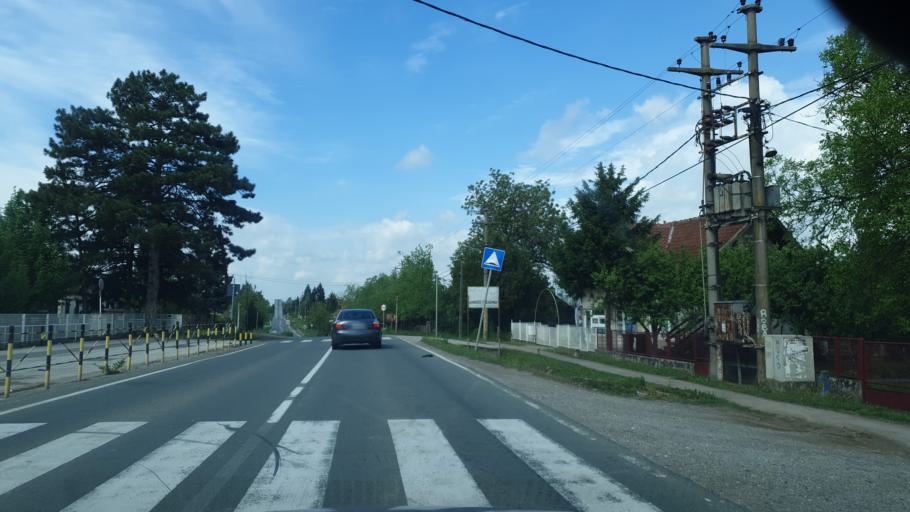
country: RS
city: Stubline
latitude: 44.5741
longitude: 20.1521
